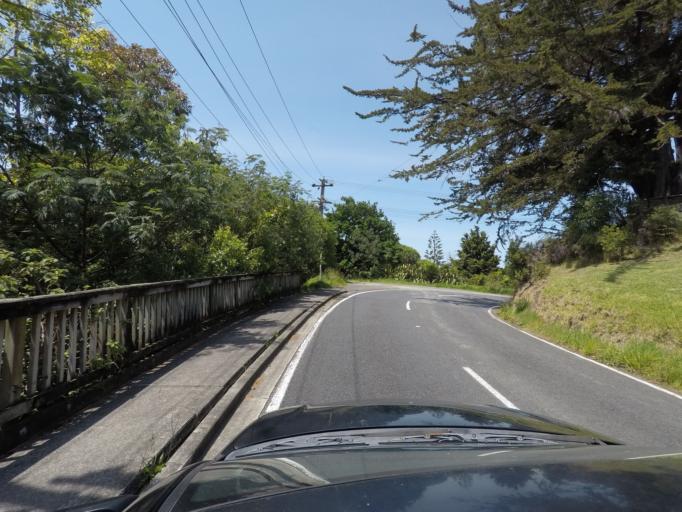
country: NZ
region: Auckland
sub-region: Auckland
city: Titirangi
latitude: -36.9656
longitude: 174.6385
